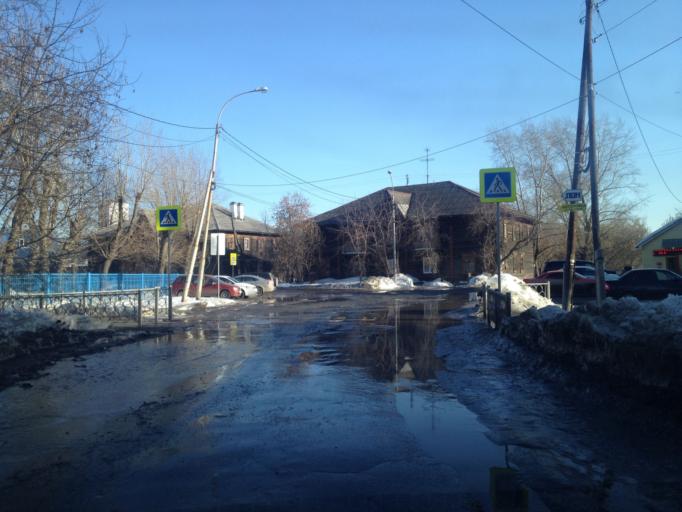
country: RU
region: Sverdlovsk
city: Yekaterinburg
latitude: 56.8617
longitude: 60.5818
